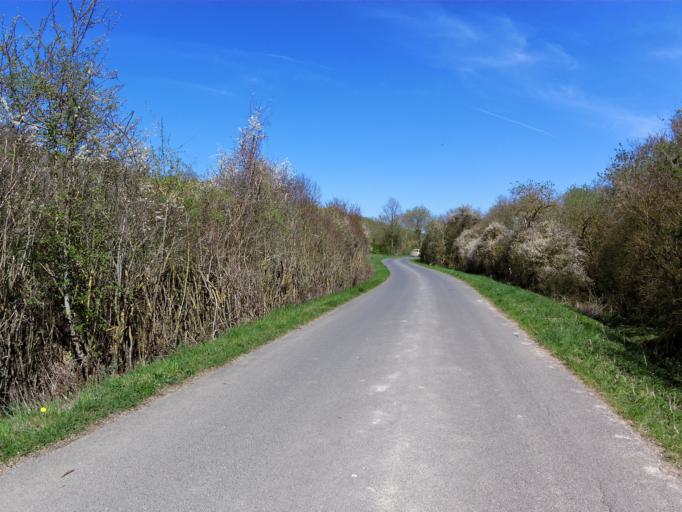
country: DE
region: Bavaria
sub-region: Regierungsbezirk Unterfranken
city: Rottendorf
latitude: 49.7951
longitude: 10.0375
